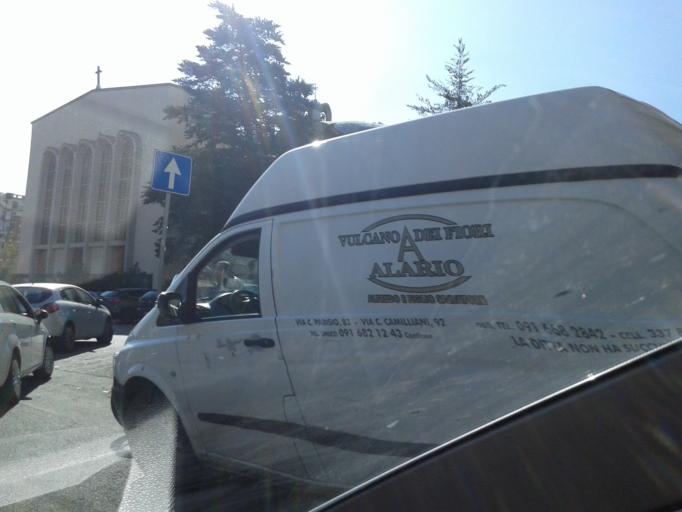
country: IT
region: Sicily
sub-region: Palermo
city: Palermo
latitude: 38.1284
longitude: 13.3339
